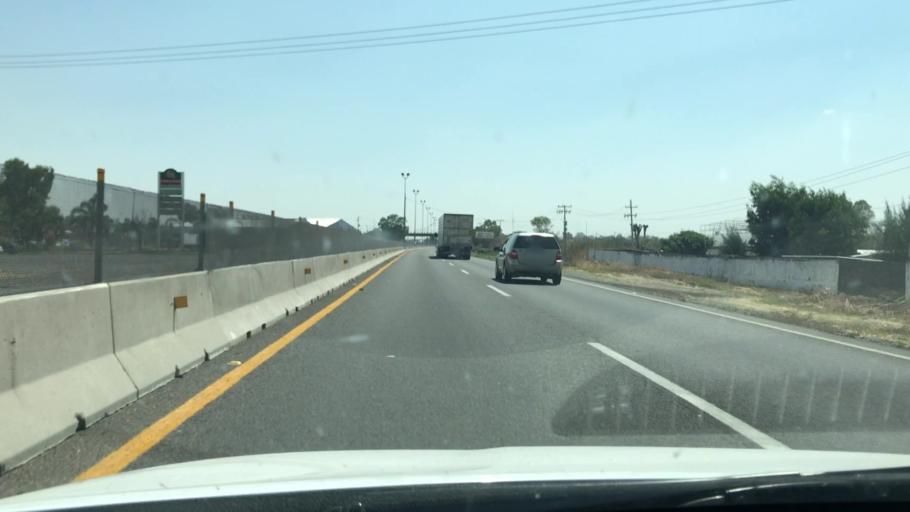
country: MX
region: Guanajuato
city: Abasolo
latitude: 20.4570
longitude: -101.5359
